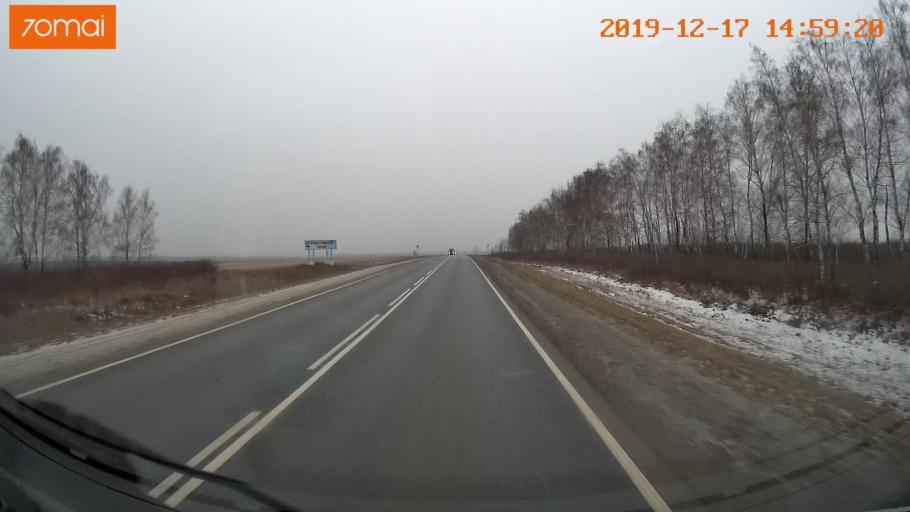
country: RU
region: Rjazan
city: Zakharovo
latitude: 54.3050
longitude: 39.2066
